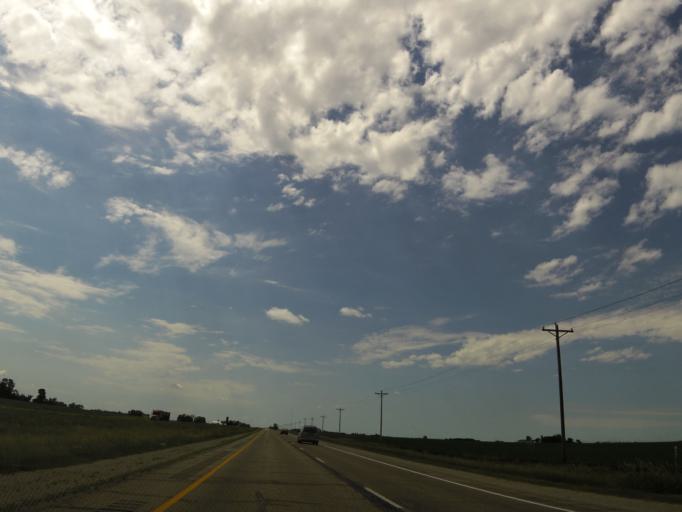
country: US
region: Iowa
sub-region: Bremer County
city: Tripoli
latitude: 42.7989
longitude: -92.3374
